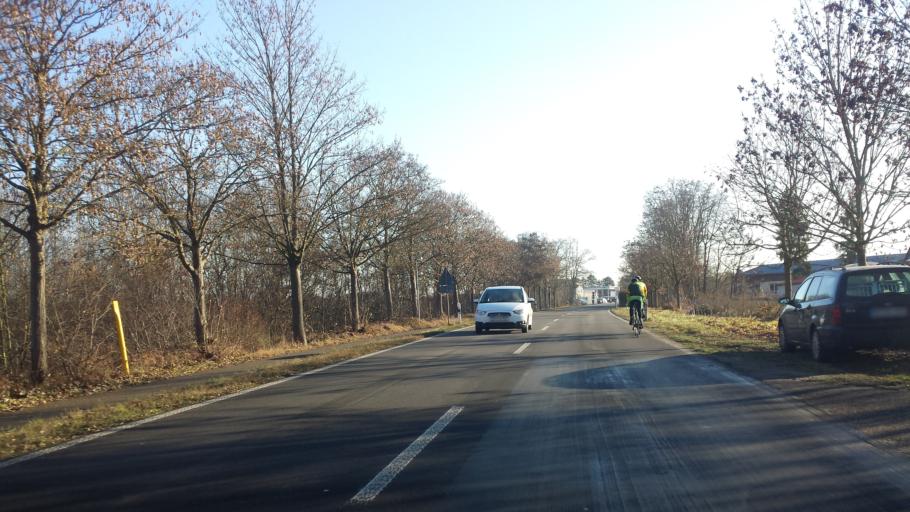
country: DE
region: Baden-Wuerttemberg
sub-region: Karlsruhe Region
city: Oberhausen-Rheinhausen
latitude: 49.2688
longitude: 8.4768
